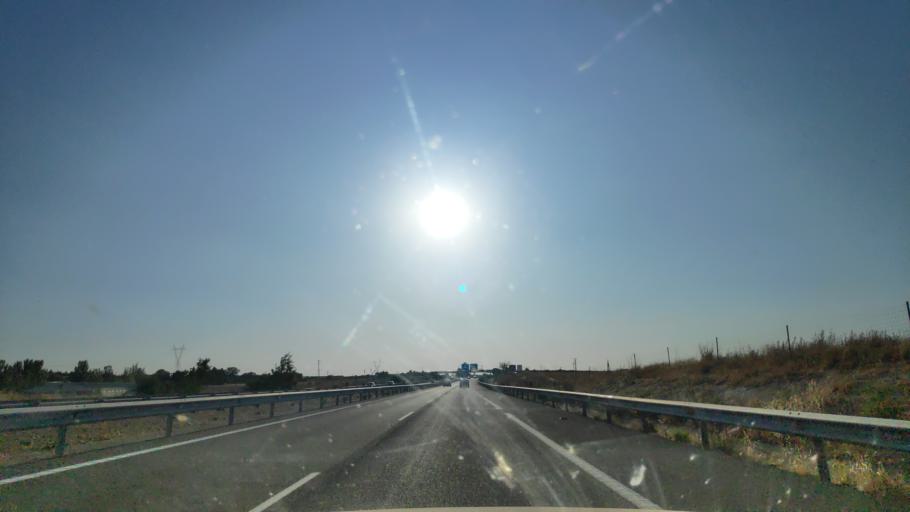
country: ES
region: Castille-La Mancha
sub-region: Provincia de Cuenca
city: Tarancon
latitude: 39.9933
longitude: -3.0002
